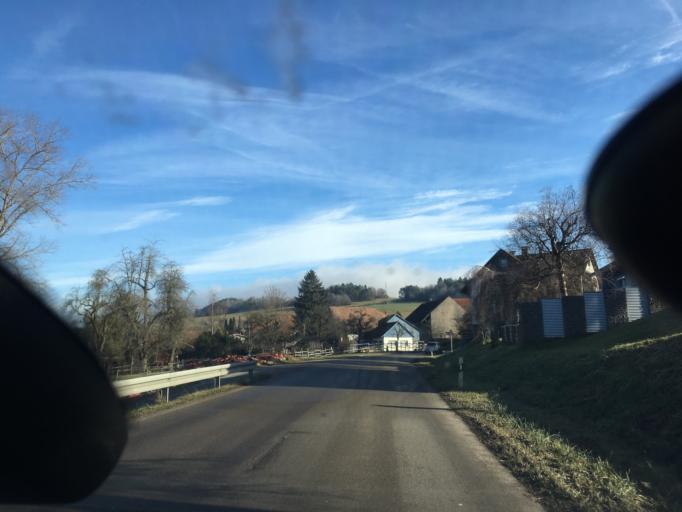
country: DE
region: Baden-Wuerttemberg
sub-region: Freiburg Region
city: Gorwihl
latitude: 47.6447
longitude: 8.1318
